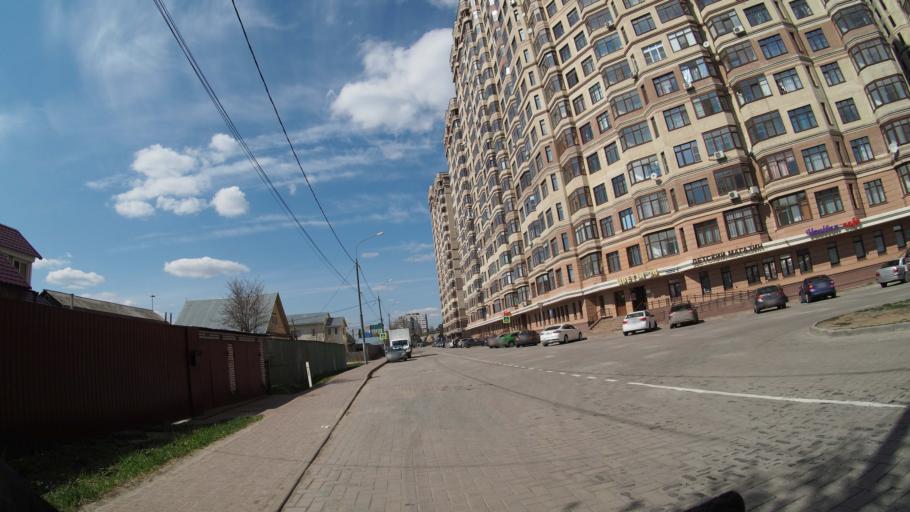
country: RU
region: Moskovskaya
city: Ramenskoye
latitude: 55.5790
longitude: 38.2139
